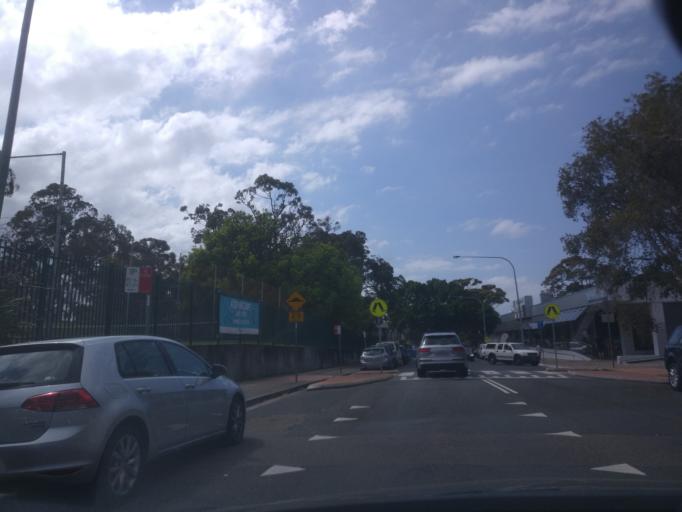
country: AU
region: New South Wales
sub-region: Pittwater
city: Warriewood
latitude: -33.6779
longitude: 151.3015
